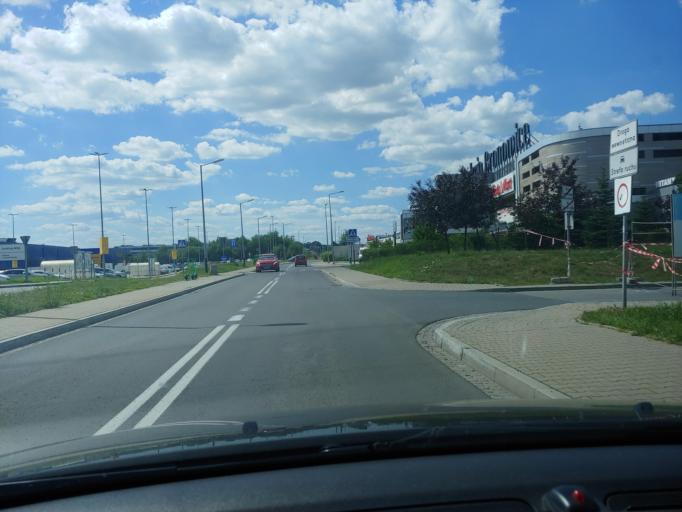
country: PL
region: Lesser Poland Voivodeship
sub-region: Powiat krakowski
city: Zielonki
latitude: 50.0904
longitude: 19.9012
